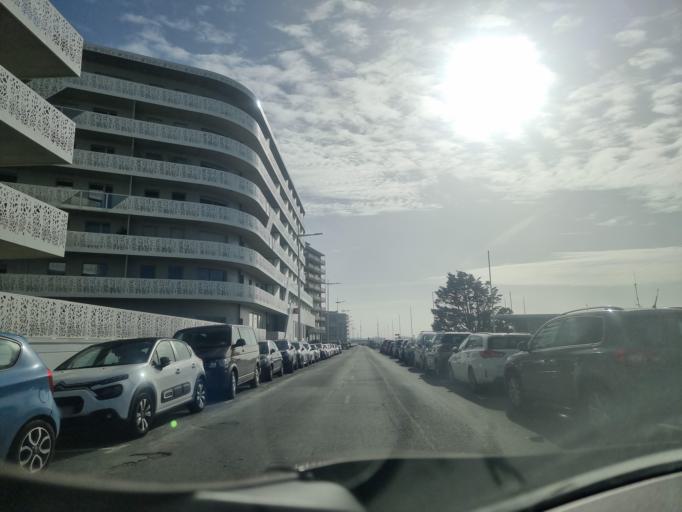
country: FR
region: Haute-Normandie
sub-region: Departement de la Seine-Maritime
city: Le Havre
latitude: 49.4907
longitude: 0.0974
